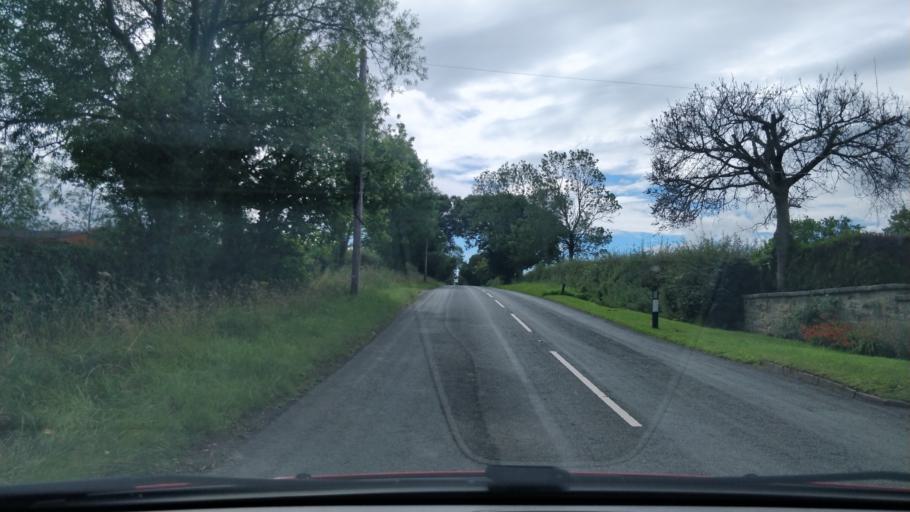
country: GB
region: Wales
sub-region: County of Flintshire
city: Hope
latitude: 53.1295
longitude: -3.0244
